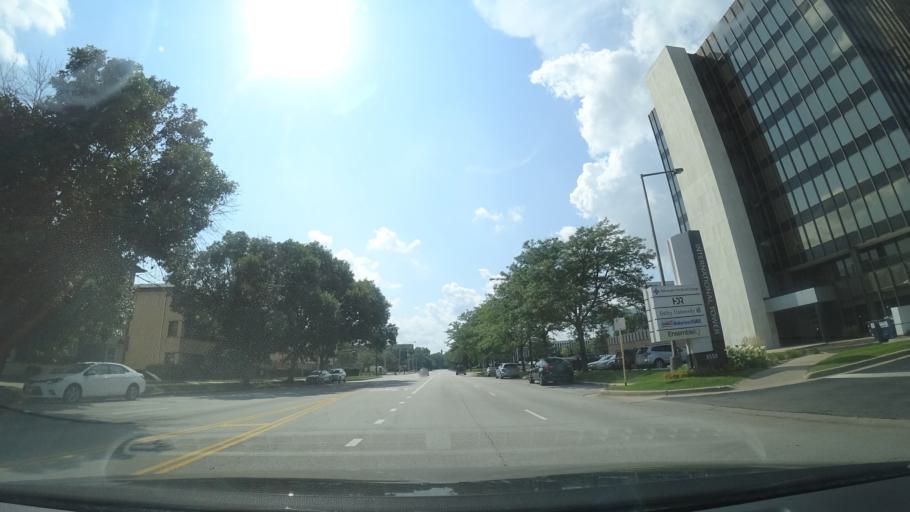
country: US
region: Illinois
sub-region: Cook County
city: Norridge
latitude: 41.9811
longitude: -87.8405
